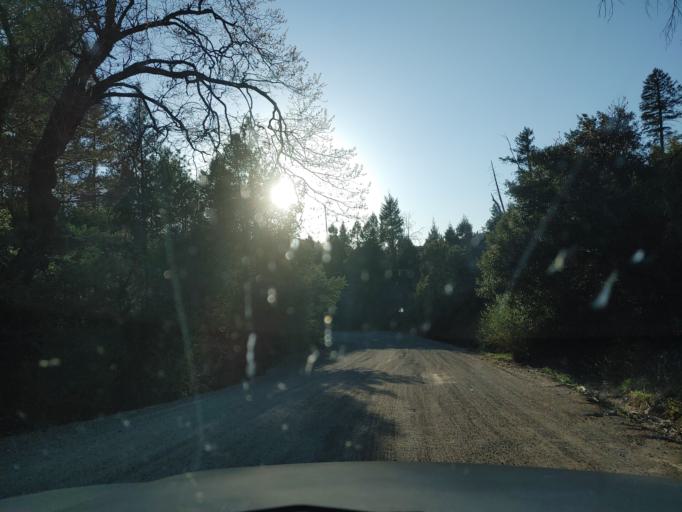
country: US
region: California
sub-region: Shasta County
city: Bella Vista
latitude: 40.8088
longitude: -121.9992
